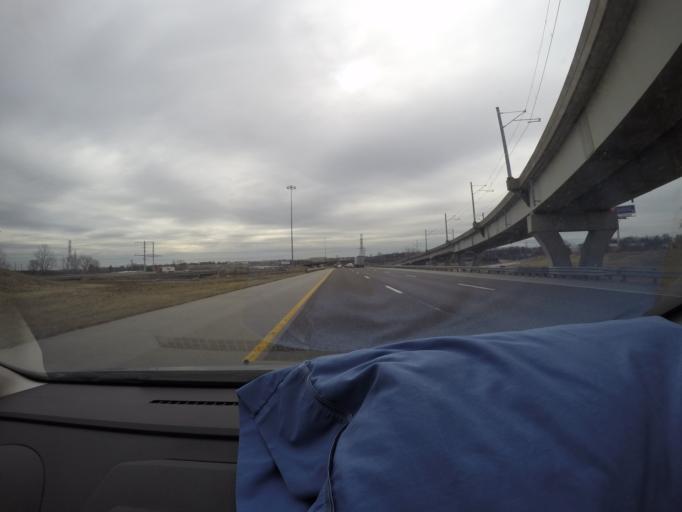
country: US
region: Missouri
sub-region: Saint Louis County
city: Saint Johns
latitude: 38.7297
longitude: -90.3338
